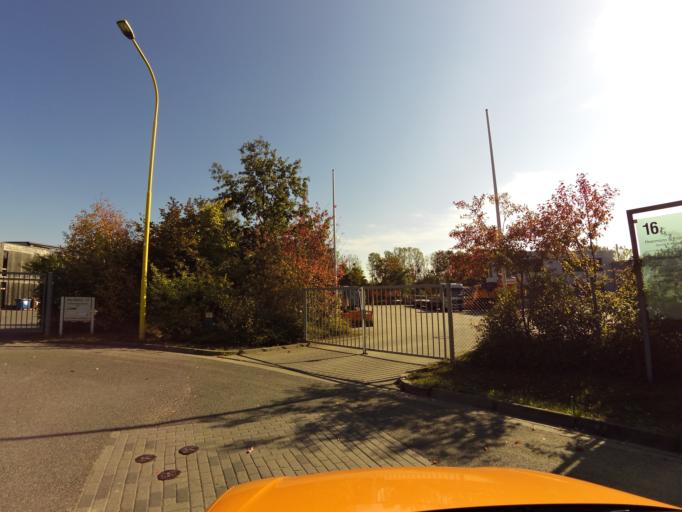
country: DE
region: Brandenburg
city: Grossbeeren
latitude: 52.3725
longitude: 13.3178
